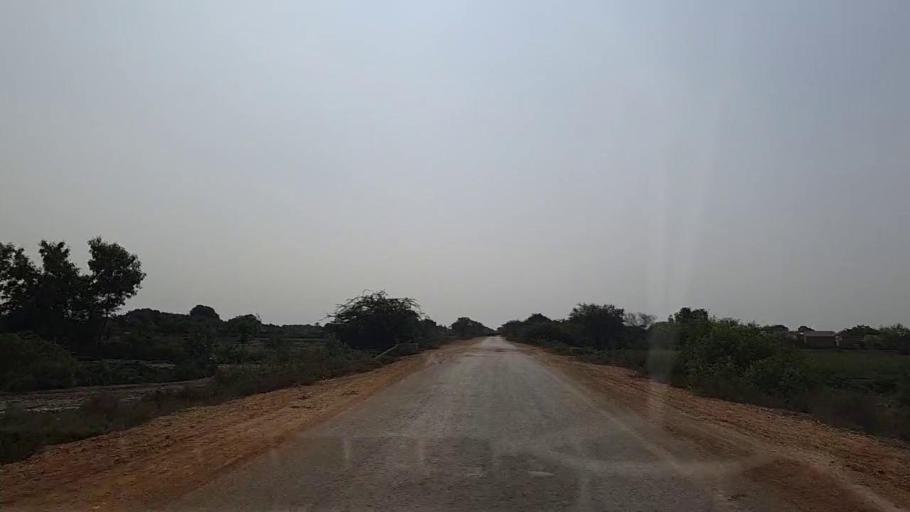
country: PK
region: Sindh
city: Chuhar Jamali
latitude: 24.2561
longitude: 67.9070
